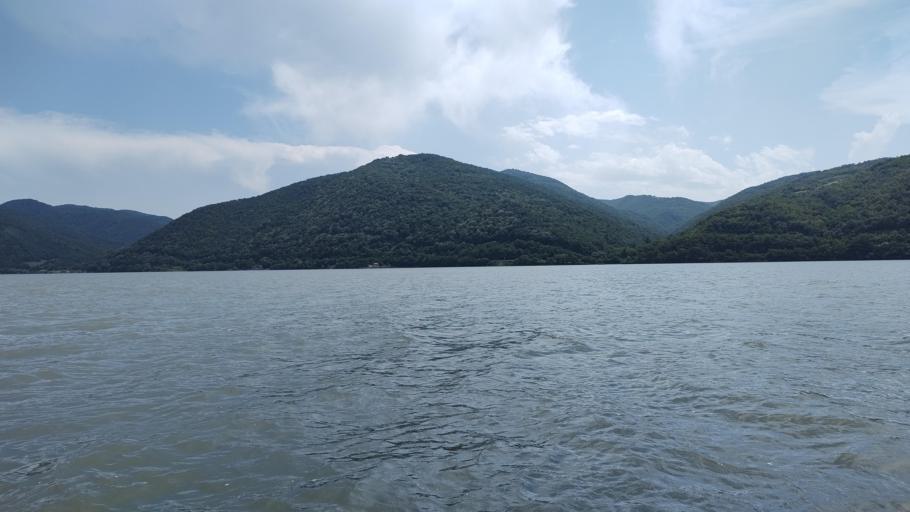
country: RO
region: Caras-Severin
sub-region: Comuna Berzasca
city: Berzasca
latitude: 44.6439
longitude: 21.9403
